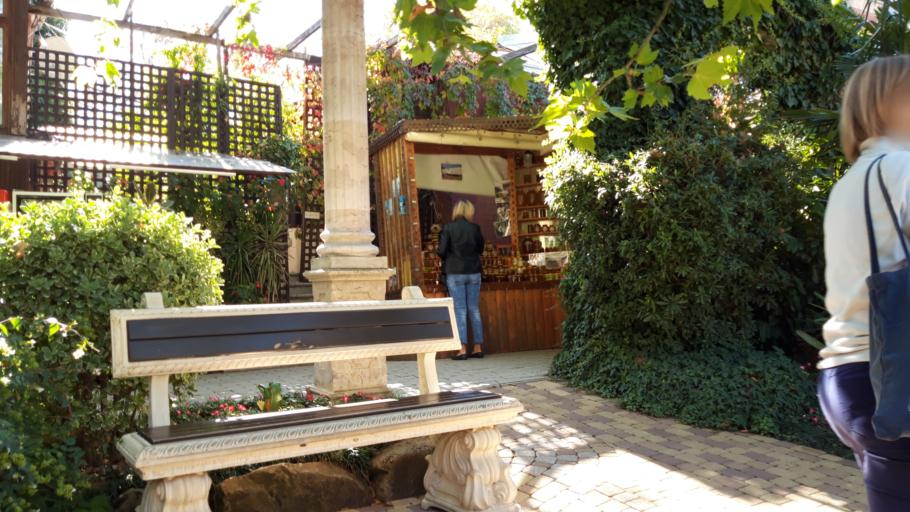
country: RU
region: Krasnodarskiy
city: Kabardinka
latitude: 44.6440
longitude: 37.9356
